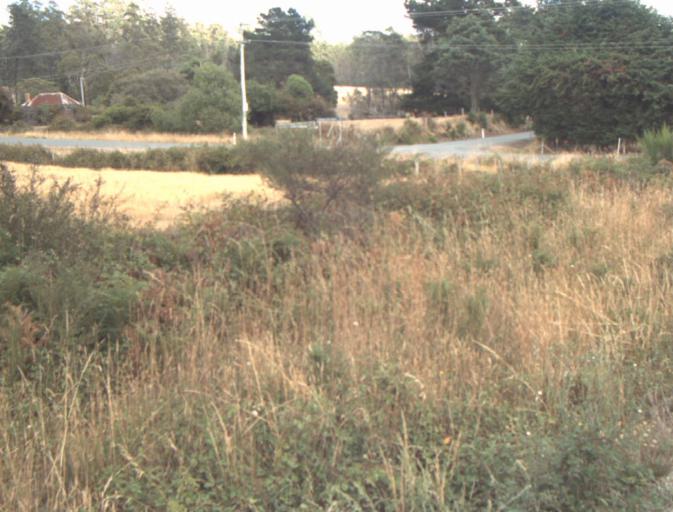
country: AU
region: Tasmania
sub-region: Launceston
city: Mayfield
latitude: -41.1976
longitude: 147.2195
